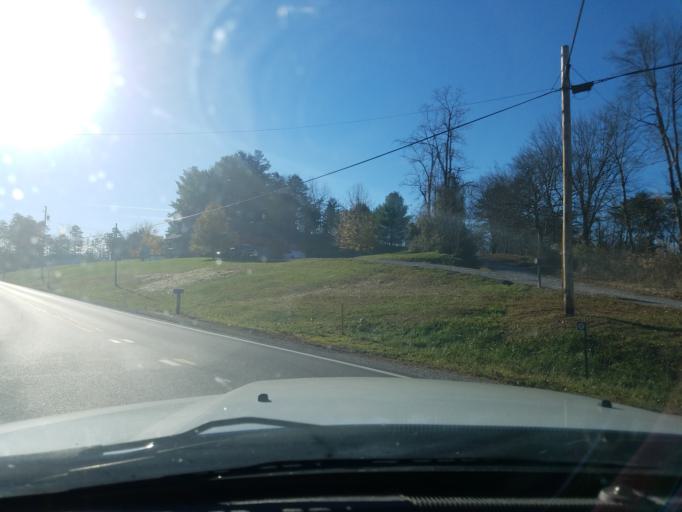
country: US
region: West Virginia
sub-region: Mason County
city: New Haven
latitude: 38.8376
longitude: -81.9223
